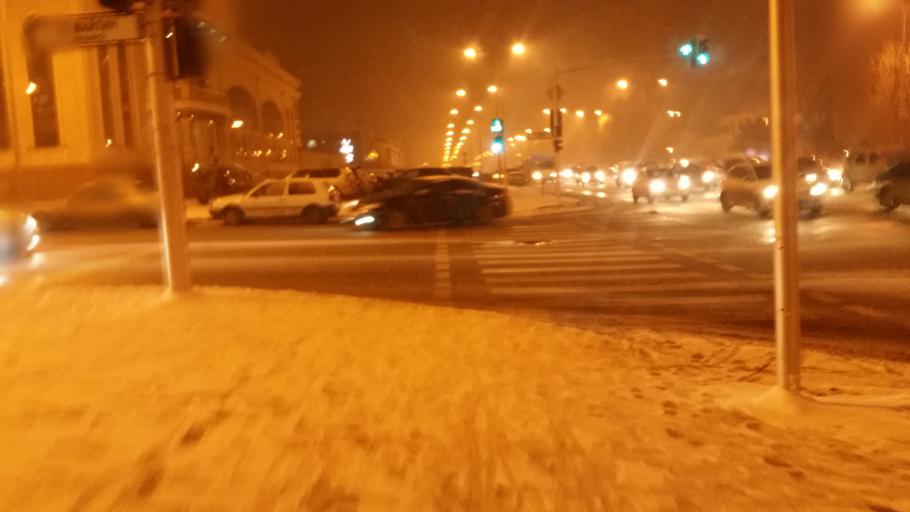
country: KZ
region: Astana Qalasy
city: Astana
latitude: 51.1479
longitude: 71.4840
